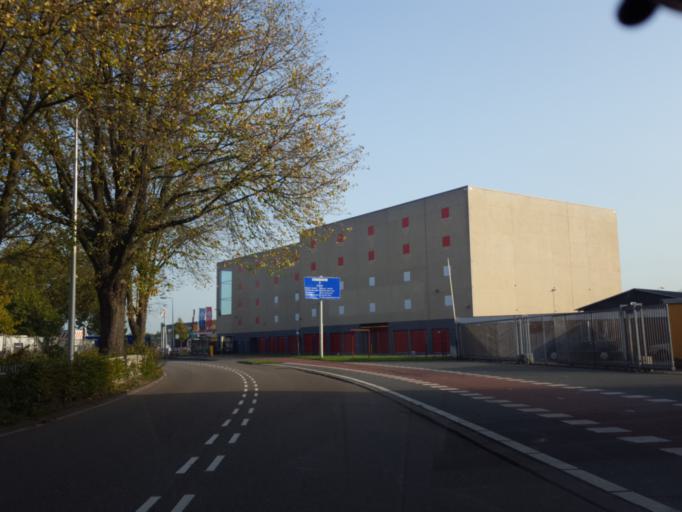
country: NL
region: Utrecht
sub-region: Gemeente Utrecht
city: Utrecht
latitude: 52.1009
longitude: 5.0842
